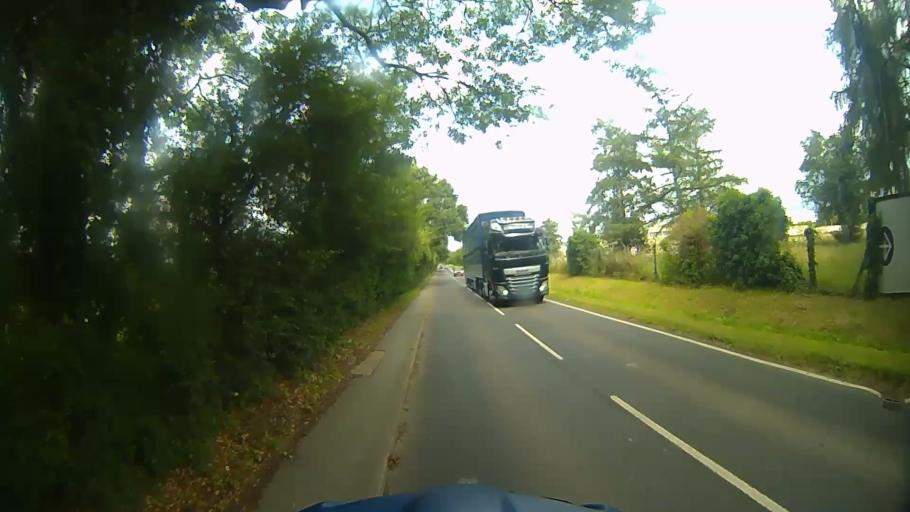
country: GB
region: England
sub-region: West Berkshire
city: Arborfield
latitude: 51.3900
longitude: -0.8995
